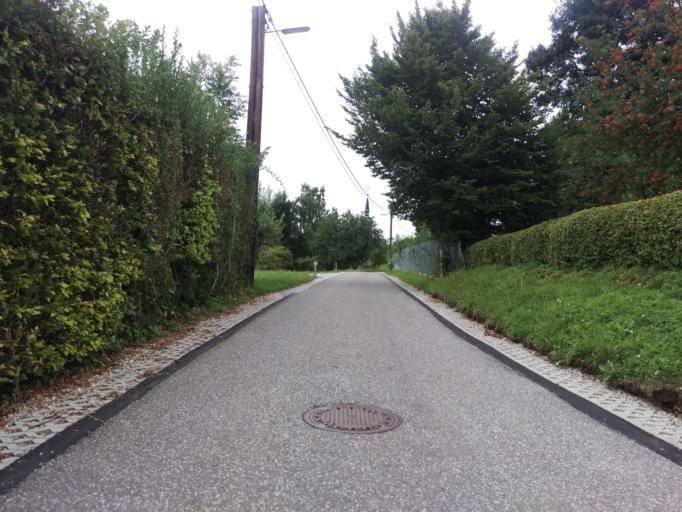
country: AT
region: Styria
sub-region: Politischer Bezirk Graz-Umgebung
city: Raaba
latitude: 47.0511
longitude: 15.4992
